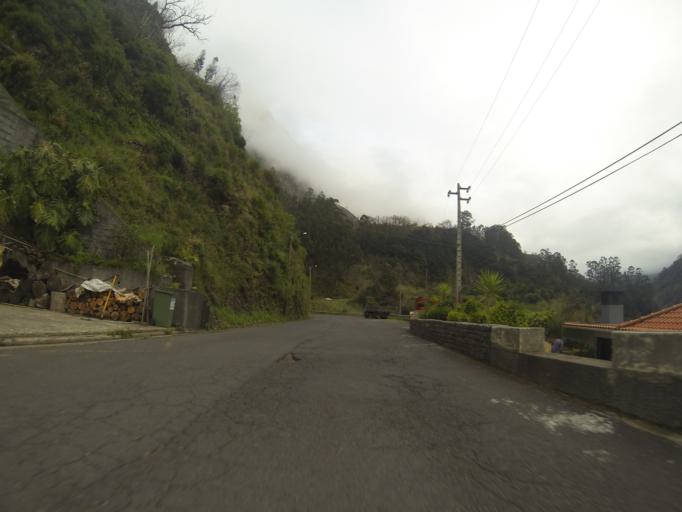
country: PT
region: Madeira
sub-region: Camara de Lobos
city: Curral das Freiras
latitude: 32.7234
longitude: -16.9668
